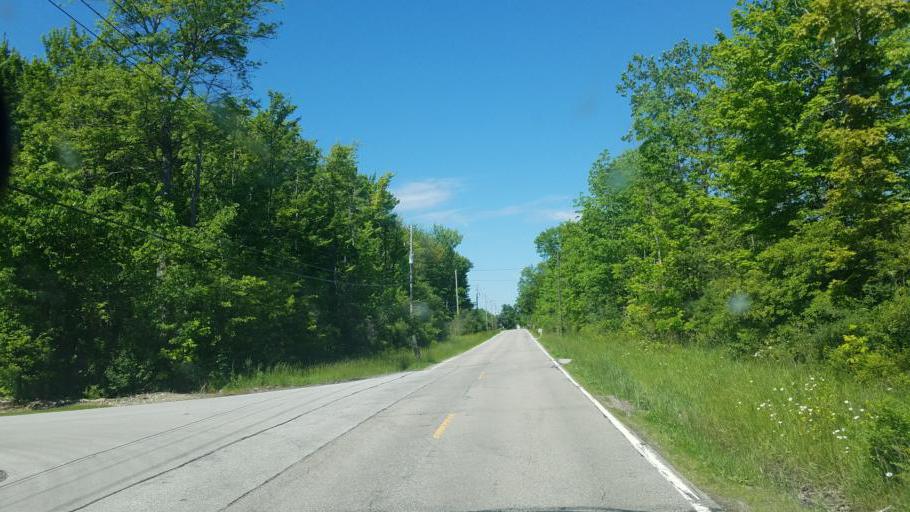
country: US
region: Ohio
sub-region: Geauga County
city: Bainbridge
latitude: 41.3695
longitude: -81.3048
